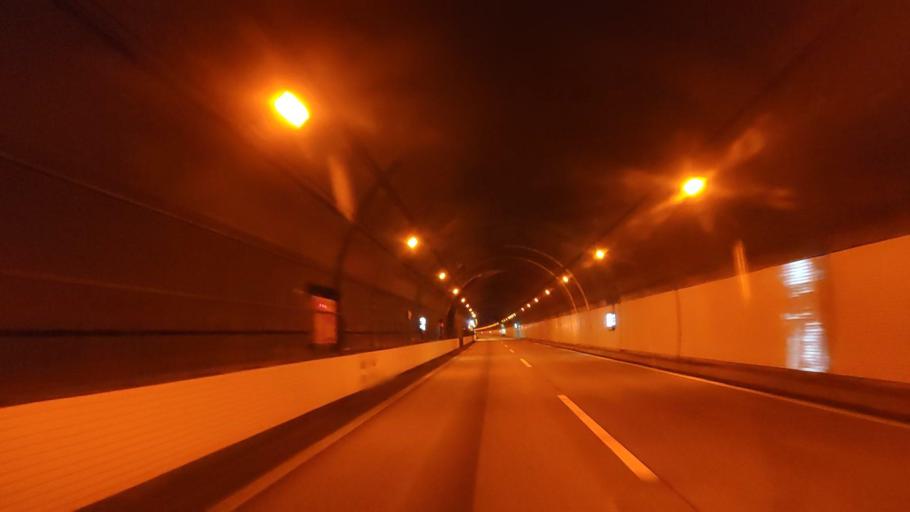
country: JP
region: Toyama
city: Nyuzen
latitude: 36.9781
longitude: 137.6586
